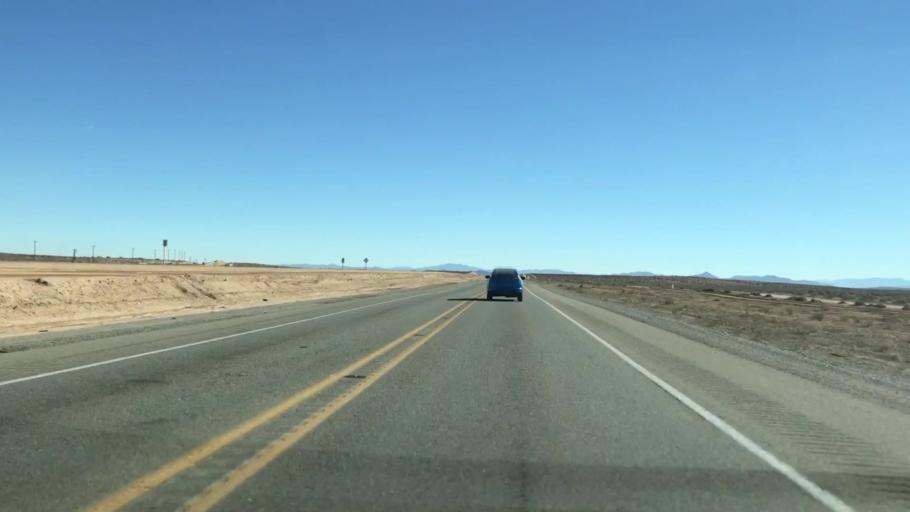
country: US
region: California
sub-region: Kern County
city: Boron
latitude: 34.9722
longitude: -117.4620
